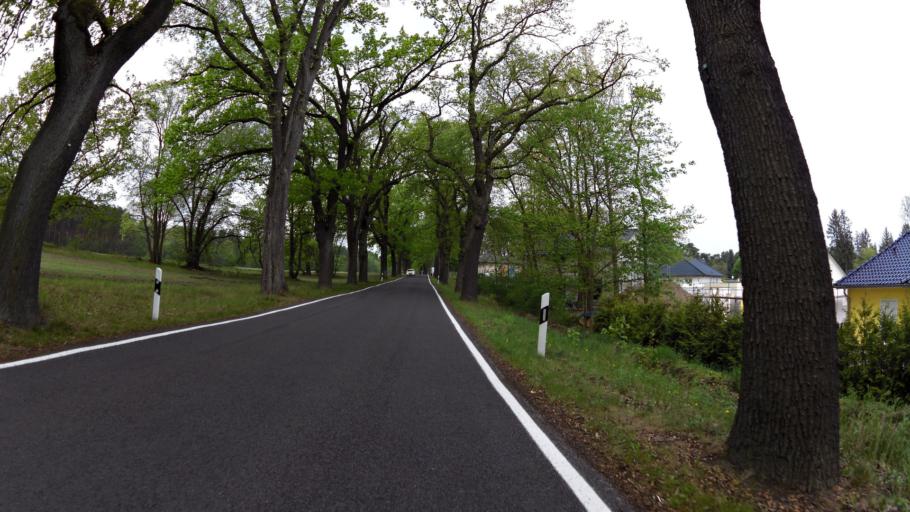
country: DE
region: Brandenburg
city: Mittenwalde
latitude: 52.2035
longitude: 13.5710
